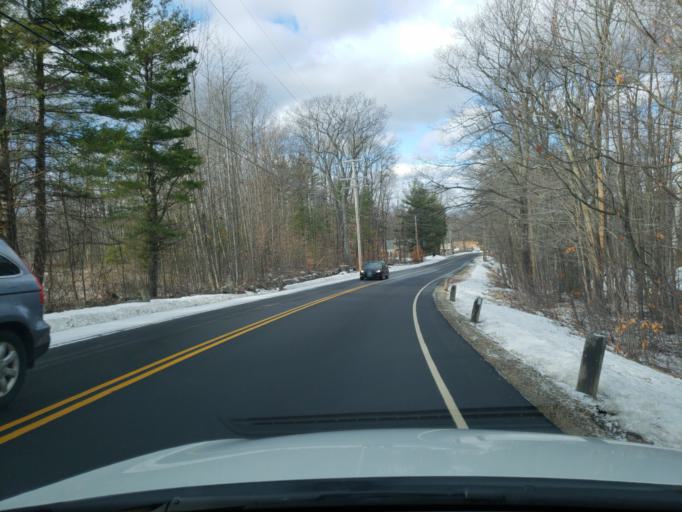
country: US
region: New Hampshire
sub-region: Hillsborough County
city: Greenfield
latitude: 43.0088
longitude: -71.8491
